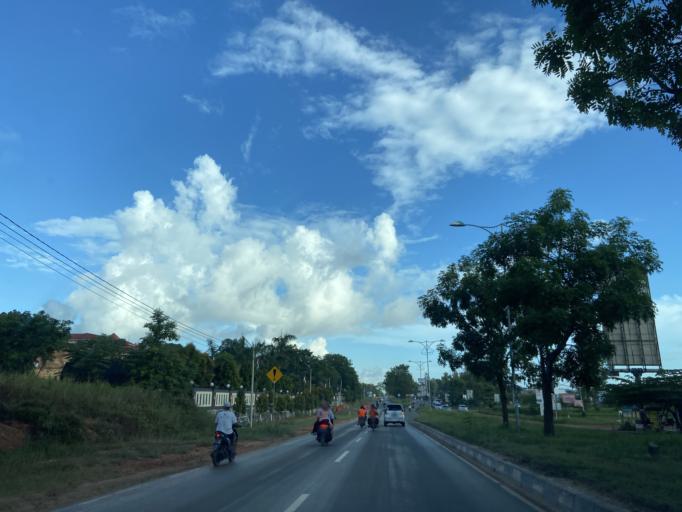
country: SG
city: Singapore
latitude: 1.0302
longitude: 104.0039
